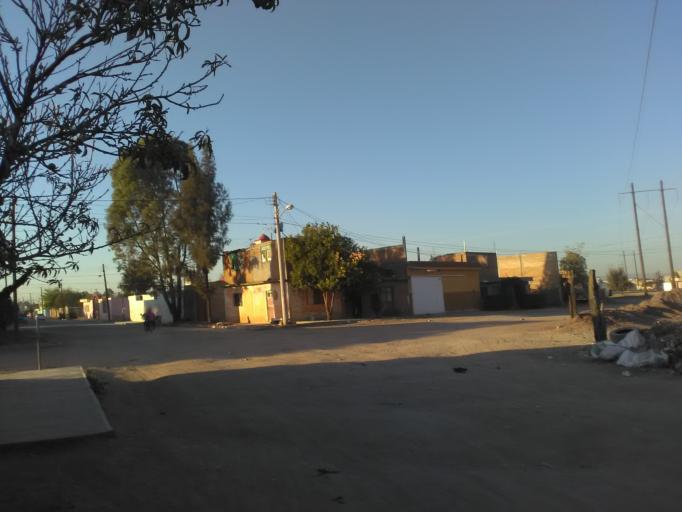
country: MX
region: Durango
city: Victoria de Durango
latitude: 24.0532
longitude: -104.6393
